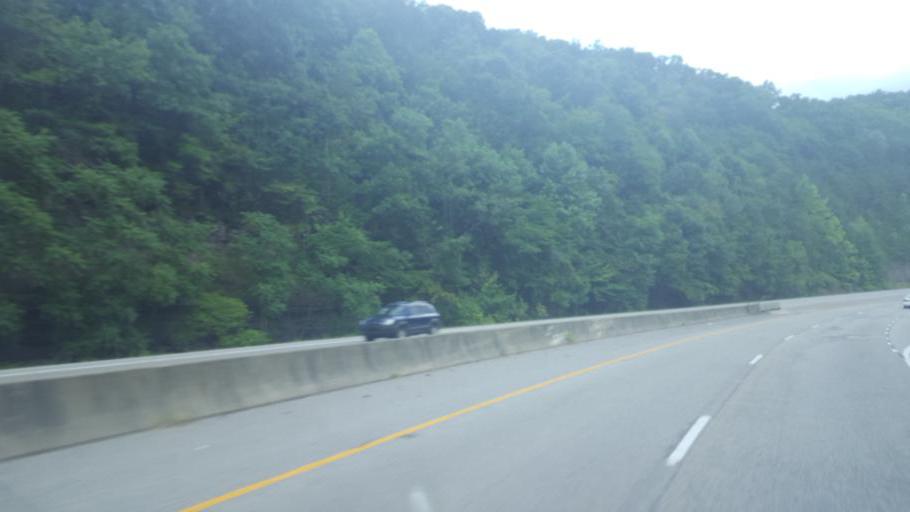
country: US
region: Kentucky
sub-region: Pike County
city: Pikeville
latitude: 37.3740
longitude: -82.5405
